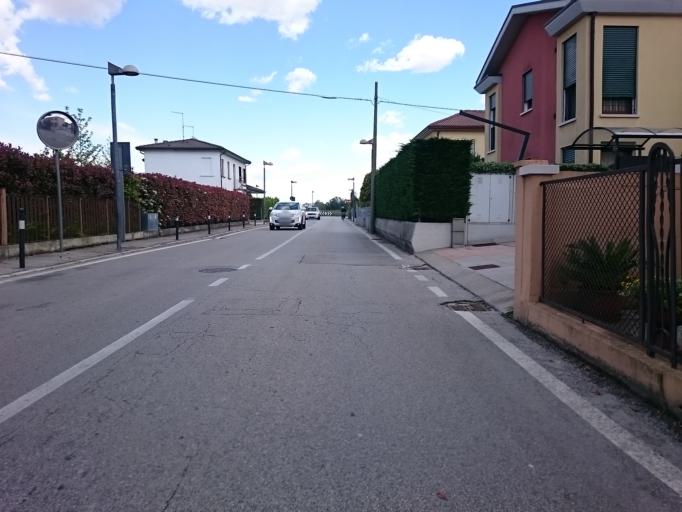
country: IT
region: Veneto
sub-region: Provincia di Padova
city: Terradura
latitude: 45.3490
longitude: 11.8207
